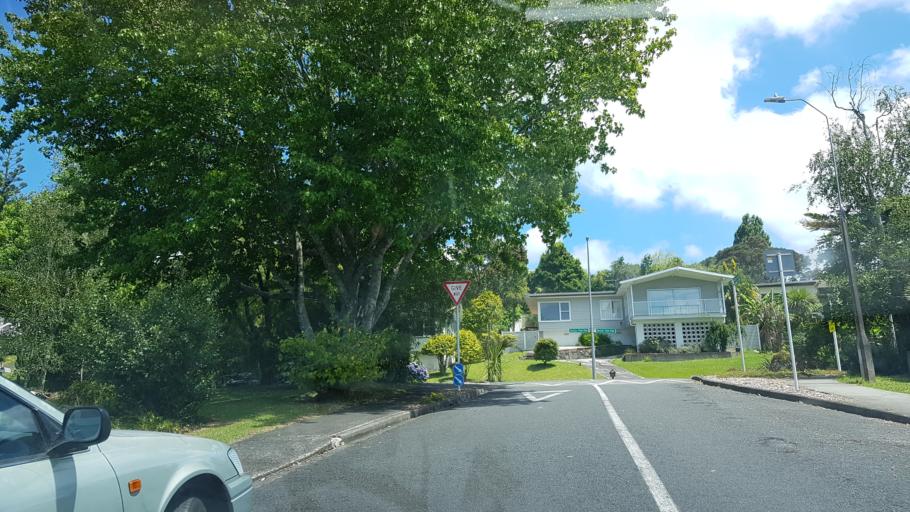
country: NZ
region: Auckland
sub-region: Auckland
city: North Shore
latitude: -36.7755
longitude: 174.7153
